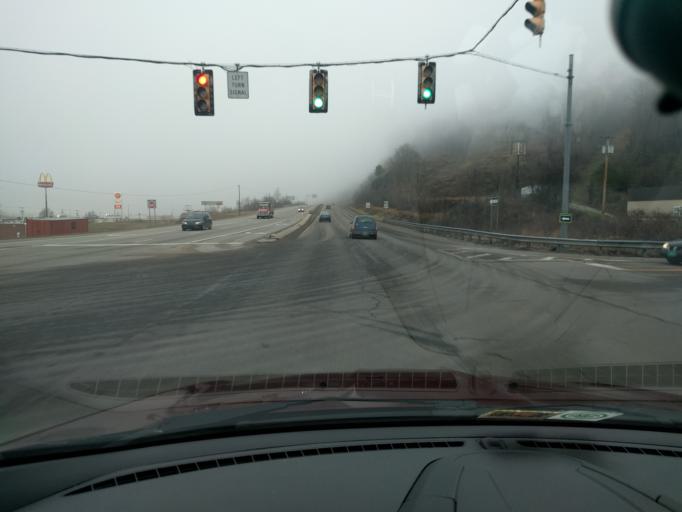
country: US
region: West Virginia
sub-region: Kanawha County
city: Chesapeake
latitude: 38.2039
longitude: -81.5022
